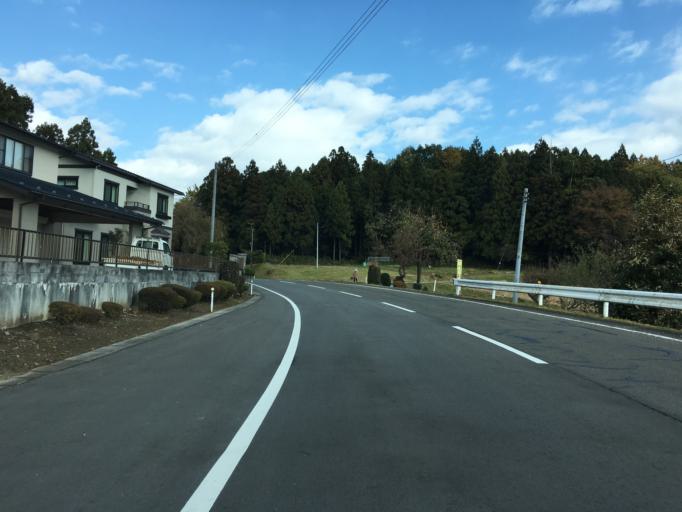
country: JP
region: Fukushima
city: Nihommatsu
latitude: 37.6310
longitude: 140.4684
